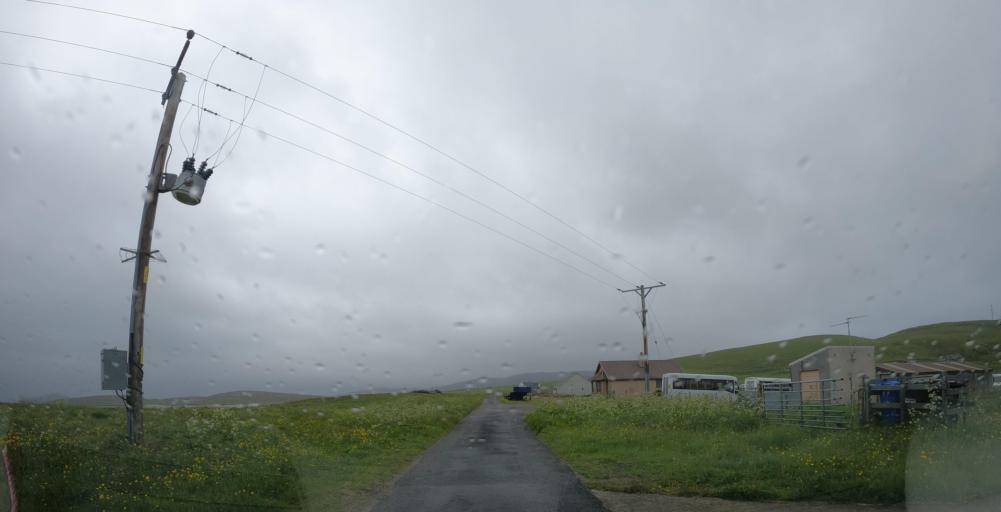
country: GB
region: Scotland
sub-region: Eilean Siar
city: Barra
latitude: 57.0397
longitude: -7.4247
